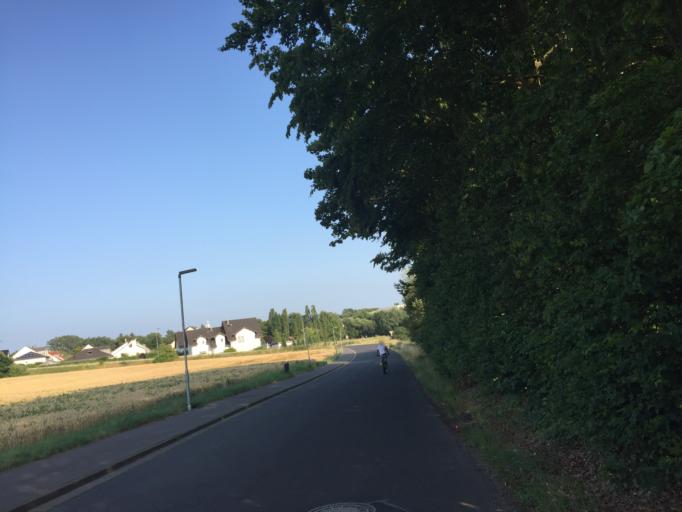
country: DE
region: Hesse
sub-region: Regierungsbezirk Giessen
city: Giessen
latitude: 50.5435
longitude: 8.7280
